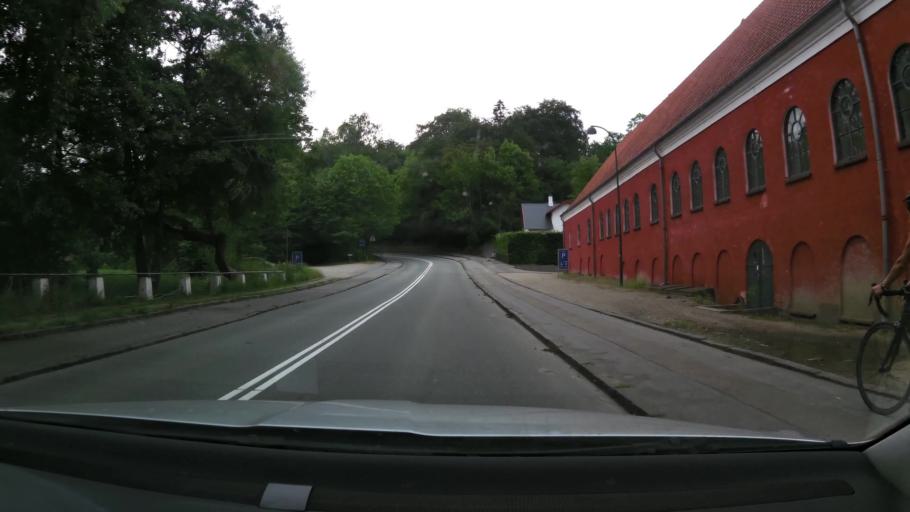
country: DK
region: Capital Region
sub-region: Lyngby-Tarbaek Kommune
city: Kongens Lyngby
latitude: 55.8001
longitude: 12.5053
